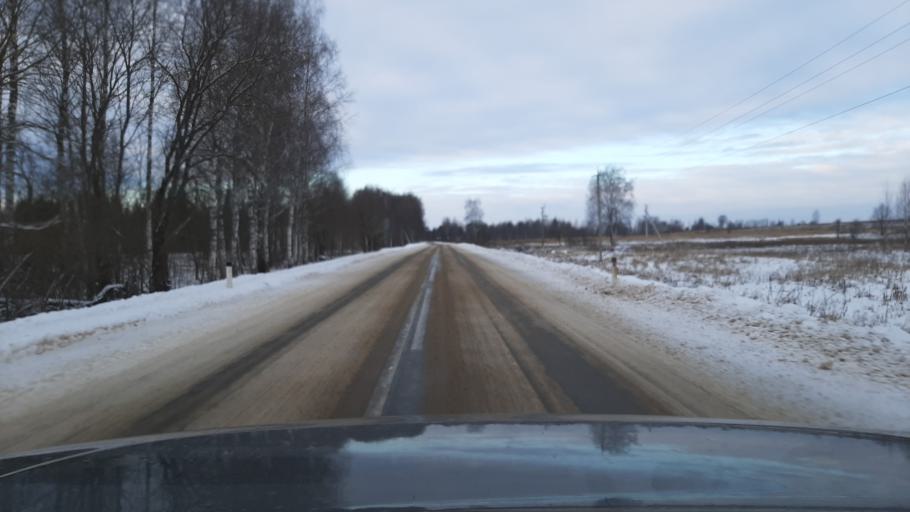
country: RU
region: Kostroma
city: Nerekhta
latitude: 57.4723
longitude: 40.6514
